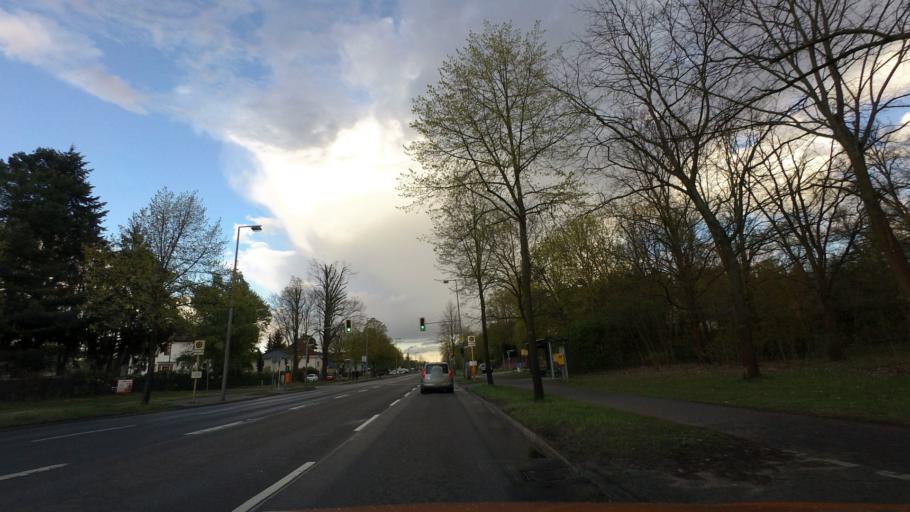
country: DE
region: Berlin
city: Staaken
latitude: 52.5265
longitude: 13.1324
